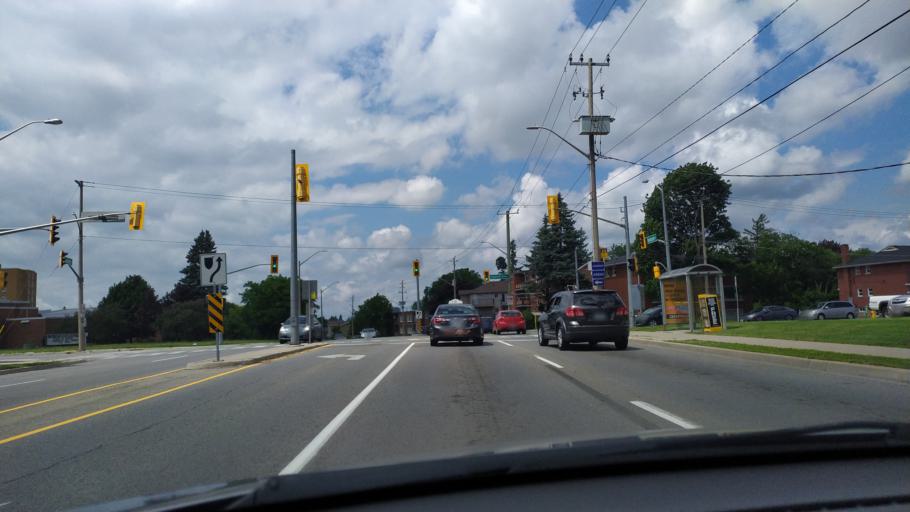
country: CA
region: Ontario
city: Kitchener
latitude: 43.4331
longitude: -80.5099
